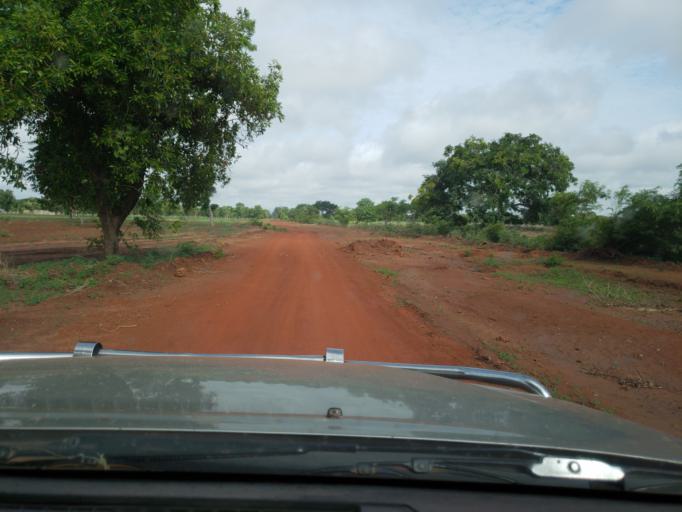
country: ML
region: Sikasso
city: Koutiala
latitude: 12.3924
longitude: -6.0063
